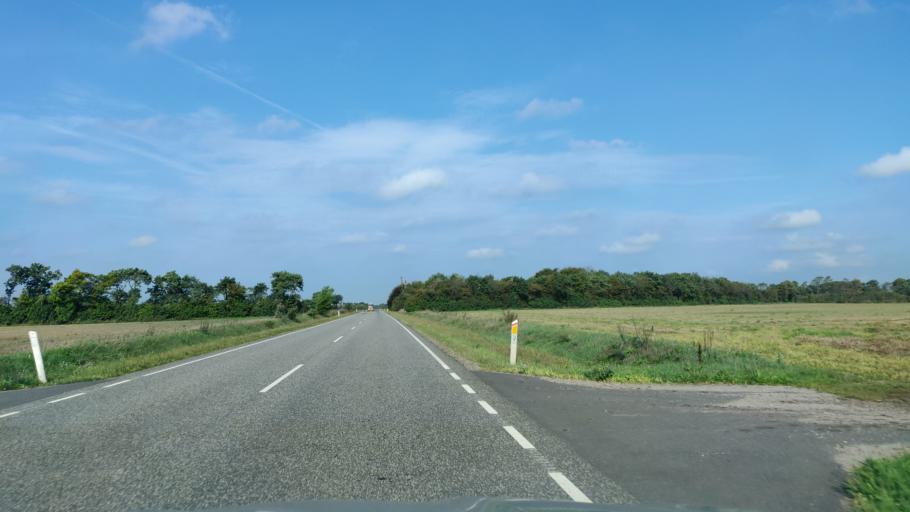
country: DK
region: Central Jutland
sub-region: Herning Kommune
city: Sunds
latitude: 56.2562
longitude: 9.0434
